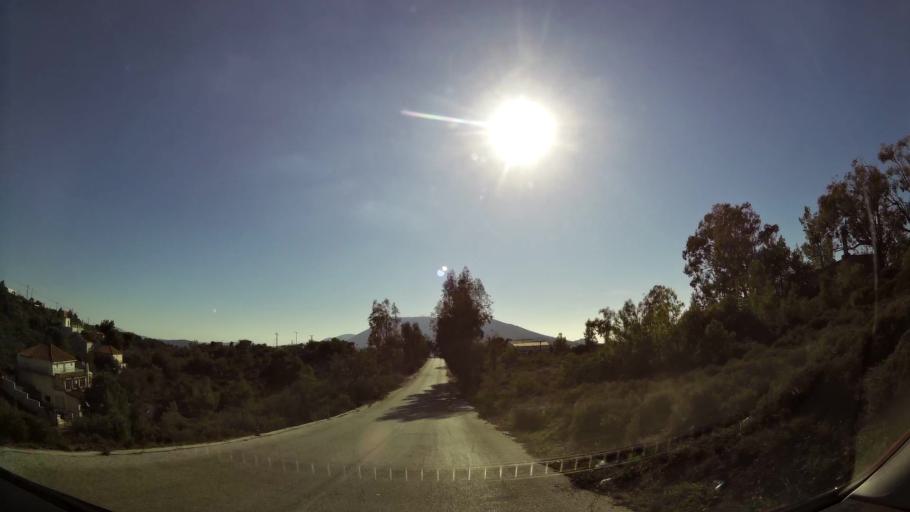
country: GR
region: Attica
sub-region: Nomarchia Anatolikis Attikis
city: Anthousa
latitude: 38.0302
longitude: 23.8714
